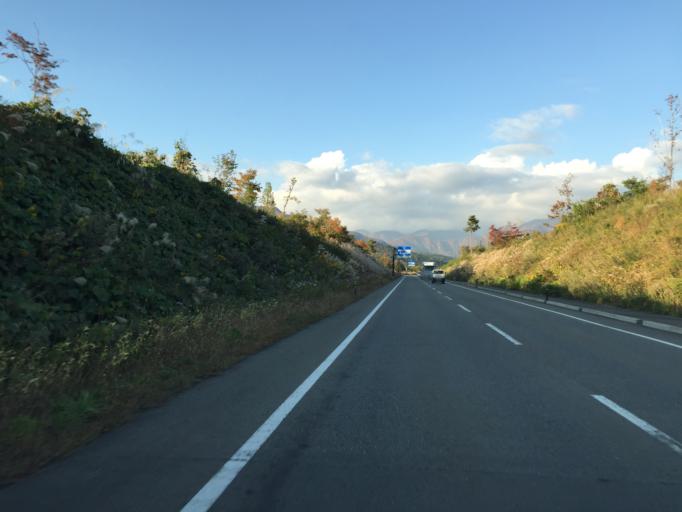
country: JP
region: Fukushima
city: Kitakata
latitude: 37.7175
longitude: 139.8693
